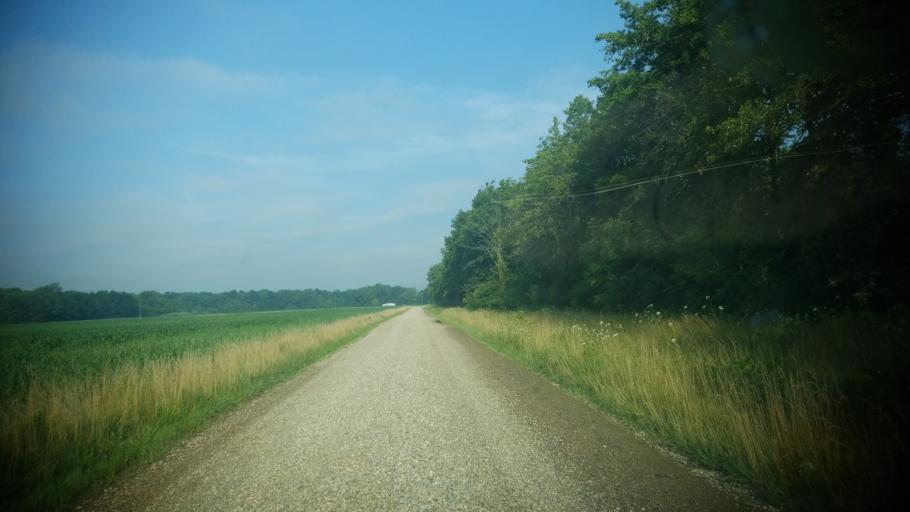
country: US
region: Illinois
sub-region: Clay County
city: Flora
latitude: 38.6020
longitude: -88.3592
